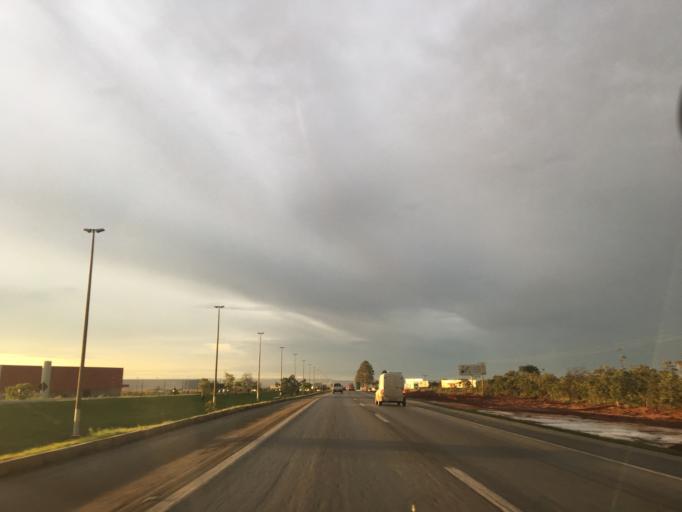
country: BR
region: Goias
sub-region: Luziania
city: Luziania
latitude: -16.0338
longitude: -47.9790
